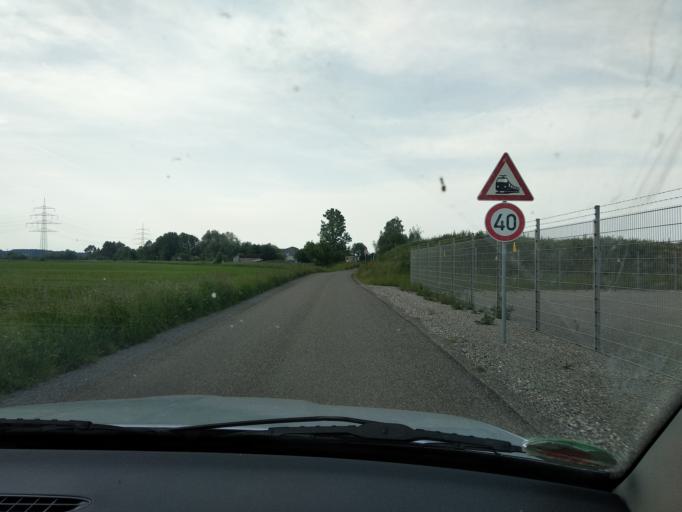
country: DE
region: Bavaria
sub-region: Swabia
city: Woringen
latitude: 47.9399
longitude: 10.2124
